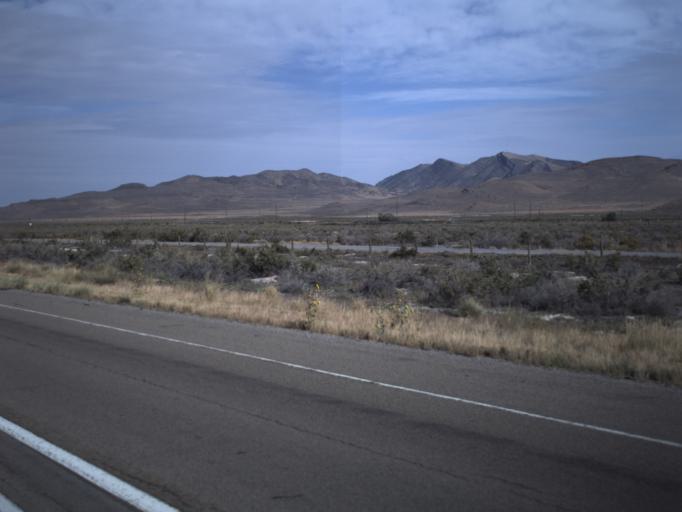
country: US
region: Utah
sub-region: Tooele County
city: Grantsville
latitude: 40.7661
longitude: -112.7871
